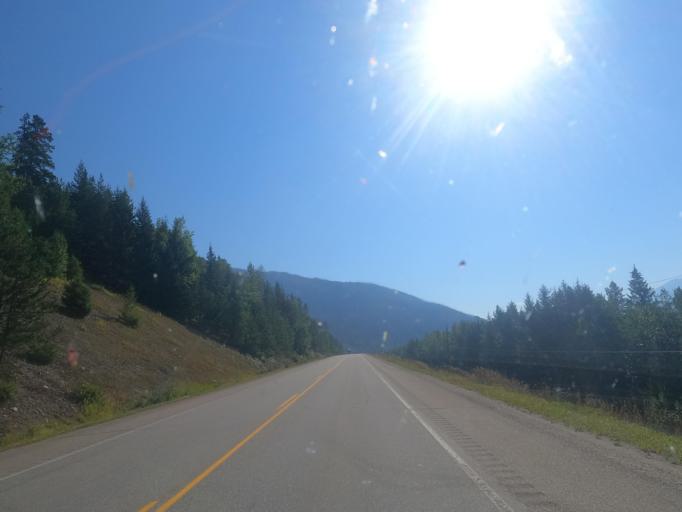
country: CA
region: Alberta
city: Jasper Park Lodge
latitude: 52.9546
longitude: -118.8835
